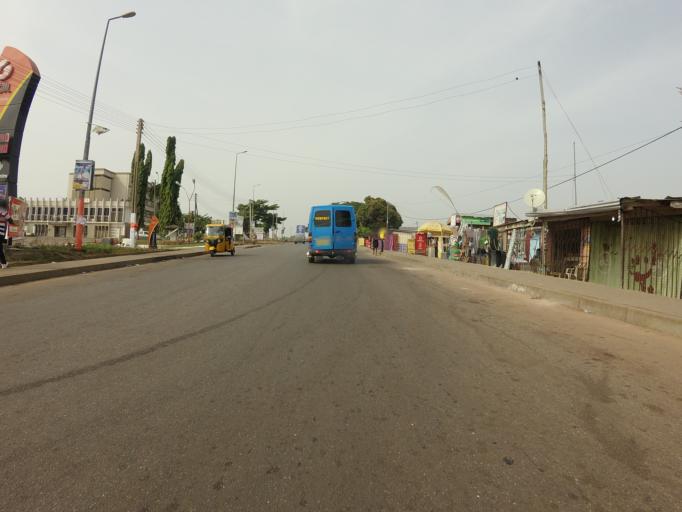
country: GH
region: Volta
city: Ho
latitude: 6.6127
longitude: 0.4640
